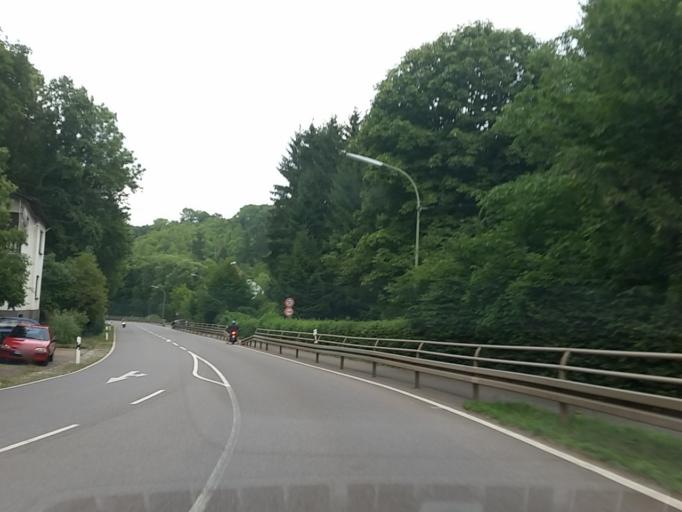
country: DE
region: Saarland
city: Schmelz
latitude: 49.4624
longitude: 6.8432
